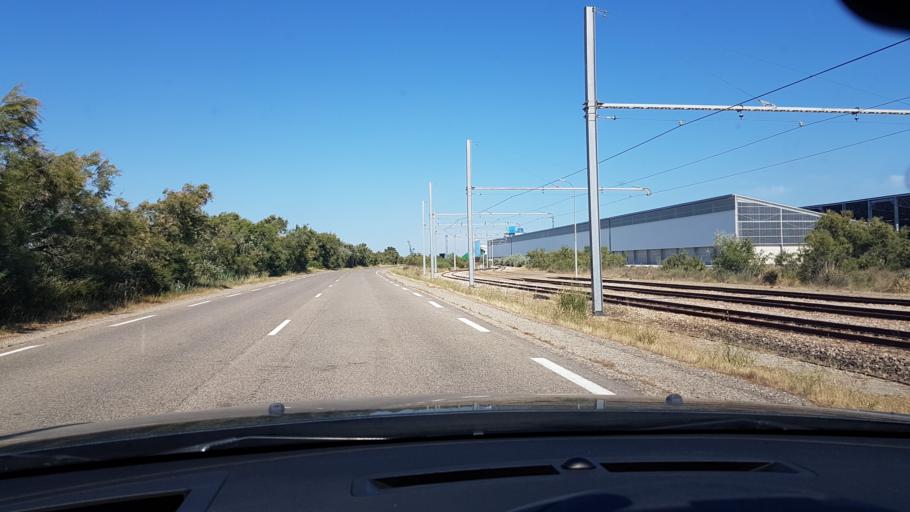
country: FR
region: Provence-Alpes-Cote d'Azur
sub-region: Departement des Bouches-du-Rhone
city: Port-Saint-Louis-du-Rhone
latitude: 43.3912
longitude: 4.8284
